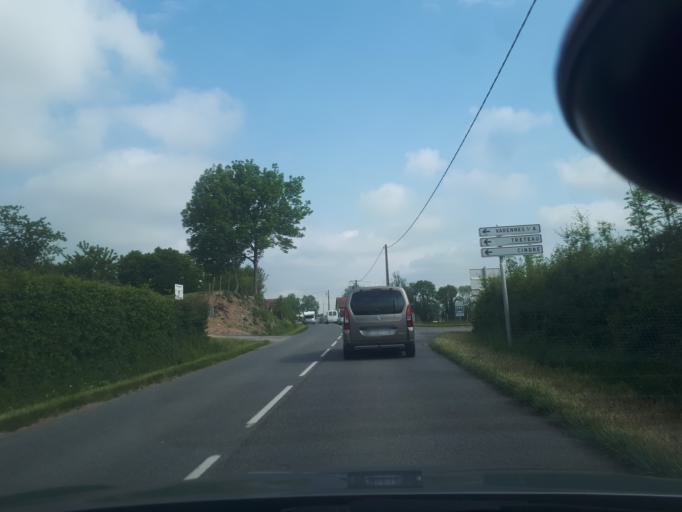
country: FR
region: Auvergne
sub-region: Departement de l'Allier
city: Lapalisse
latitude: 46.3279
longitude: 3.5842
